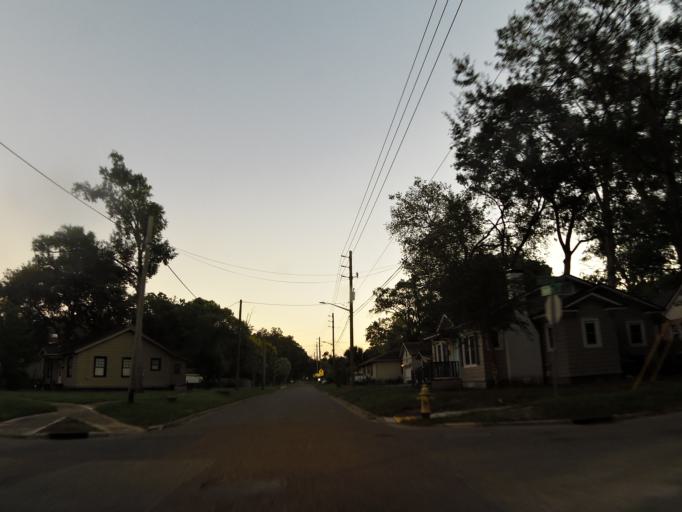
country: US
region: Florida
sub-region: Duval County
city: Jacksonville
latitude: 30.3084
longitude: -81.7222
